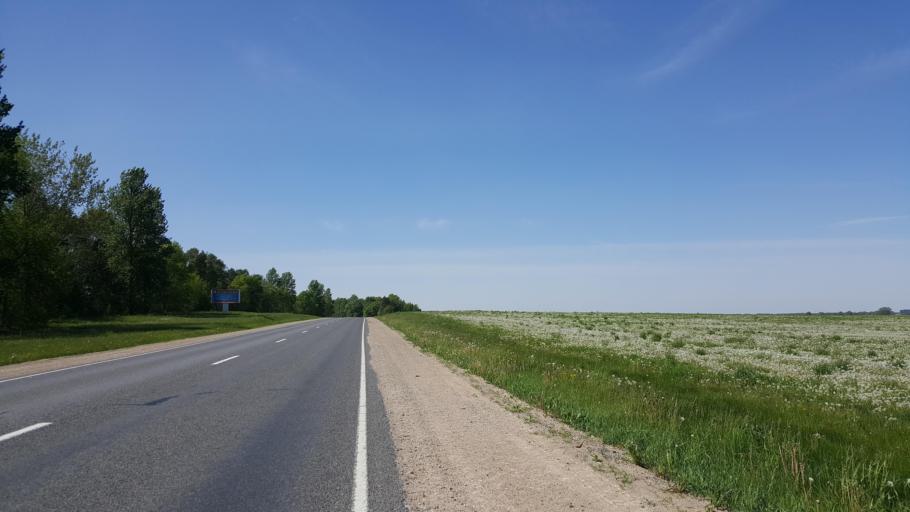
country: BY
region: Brest
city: Kamyanyets
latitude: 52.3624
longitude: 23.7817
